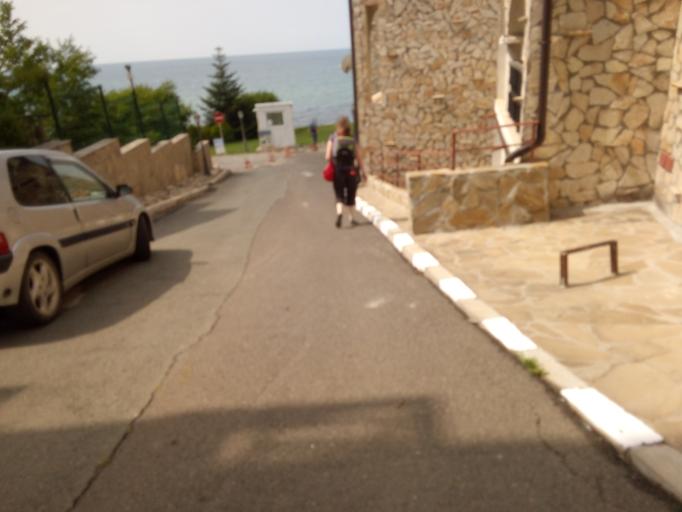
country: BG
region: Burgas
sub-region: Obshtina Nesebur
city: Sveti Vlas
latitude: 42.7061
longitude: 27.7769
